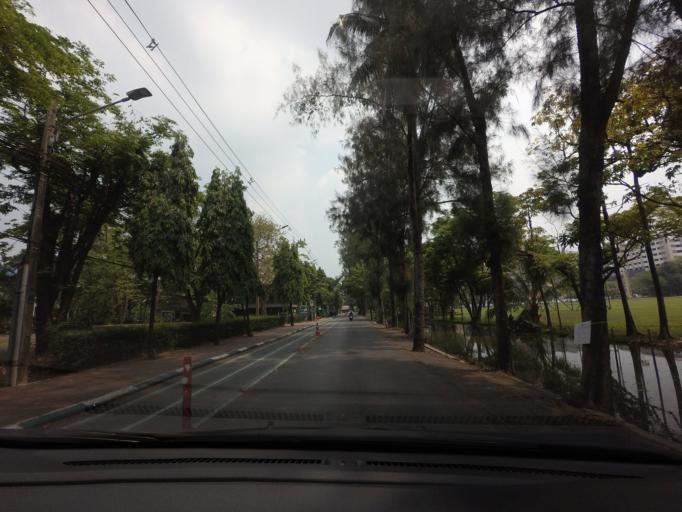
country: TH
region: Bangkok
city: Chatuchak
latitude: 13.8477
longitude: 100.5669
